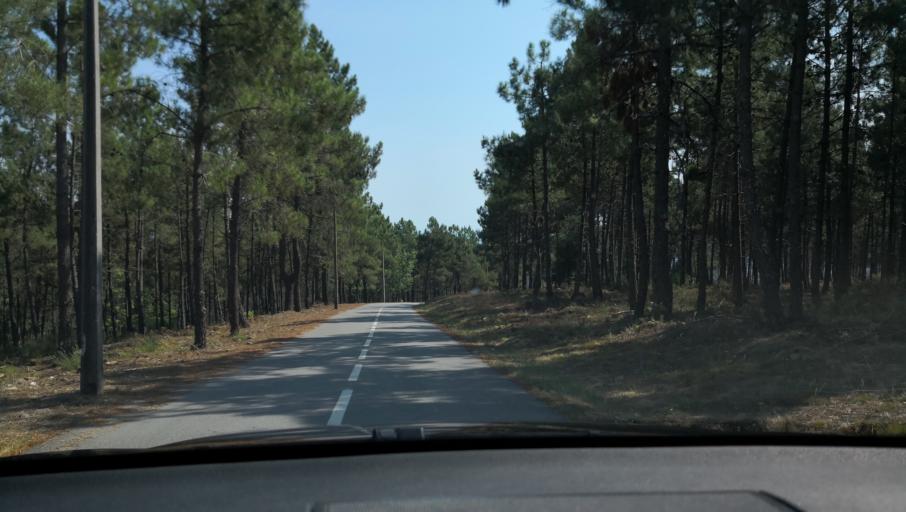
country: PT
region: Vila Real
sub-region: Sabrosa
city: Sabrosa
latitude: 41.2751
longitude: -7.6193
